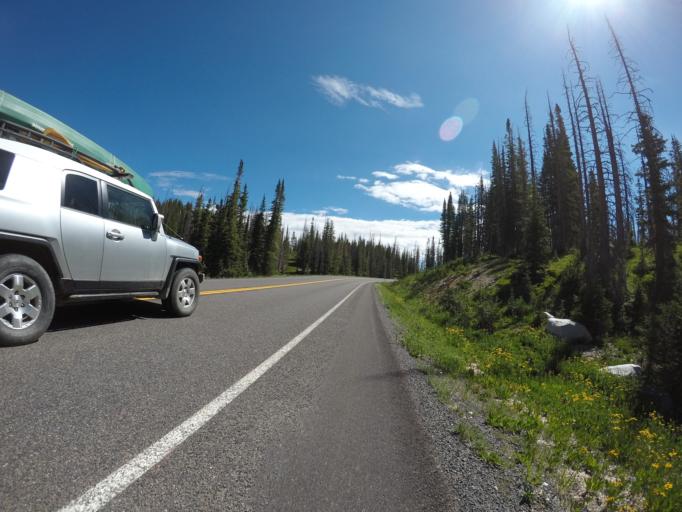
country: US
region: Wyoming
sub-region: Carbon County
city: Saratoga
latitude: 41.3250
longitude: -106.3273
